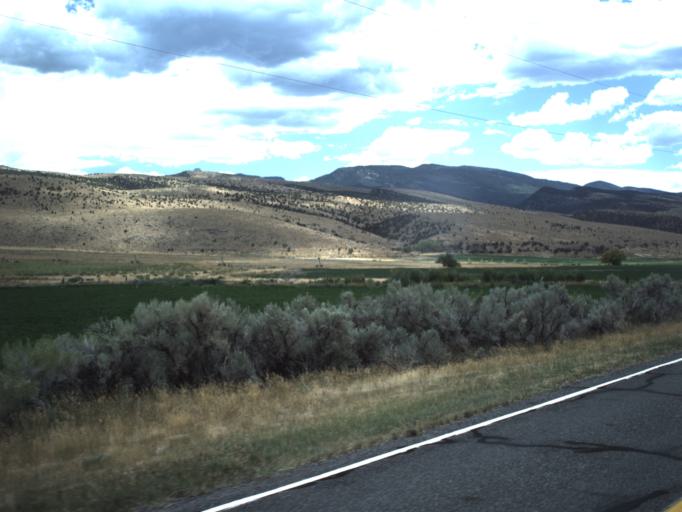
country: US
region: Utah
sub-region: Sanpete County
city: Gunnison
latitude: 39.1495
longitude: -111.7092
